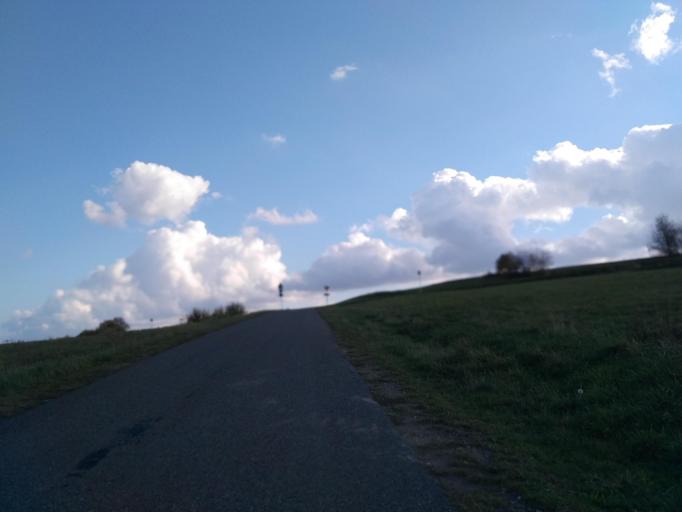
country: PL
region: Subcarpathian Voivodeship
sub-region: Powiat rzeszowski
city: Zglobien
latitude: 49.9849
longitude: 21.8482
